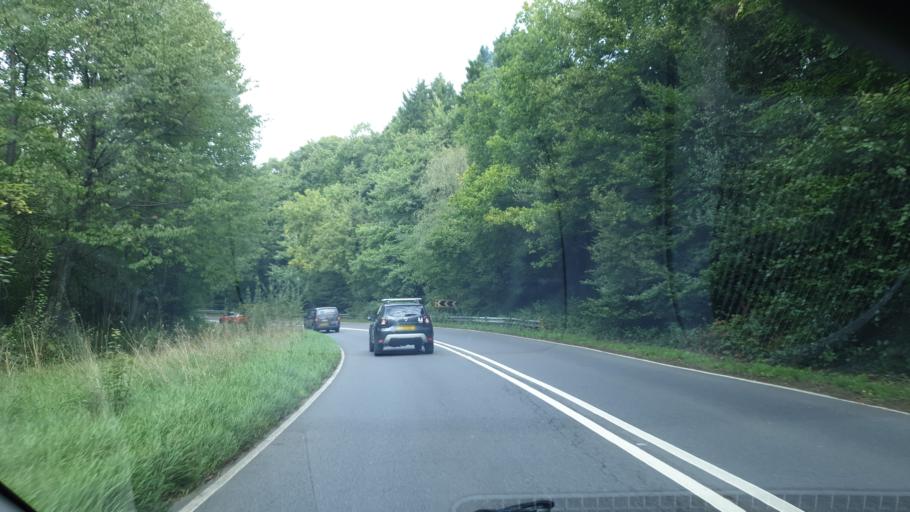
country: GB
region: England
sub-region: East Sussex
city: Forest Row
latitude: 51.1079
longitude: 0.0251
